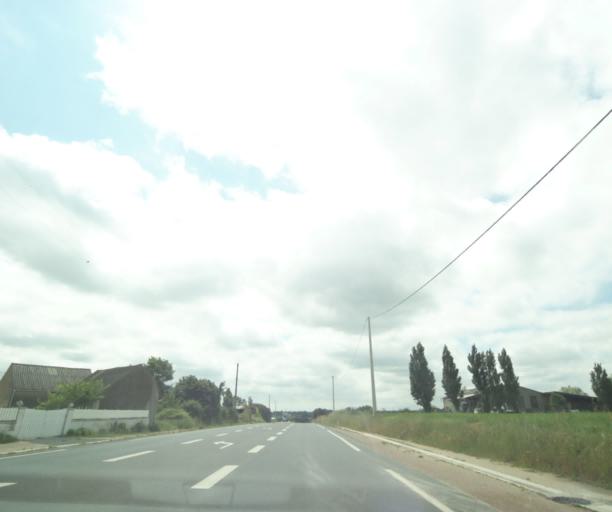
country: FR
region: Poitou-Charentes
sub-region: Departement des Deux-Sevres
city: Saint-Jean-de-Thouars
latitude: 46.9244
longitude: -0.1978
